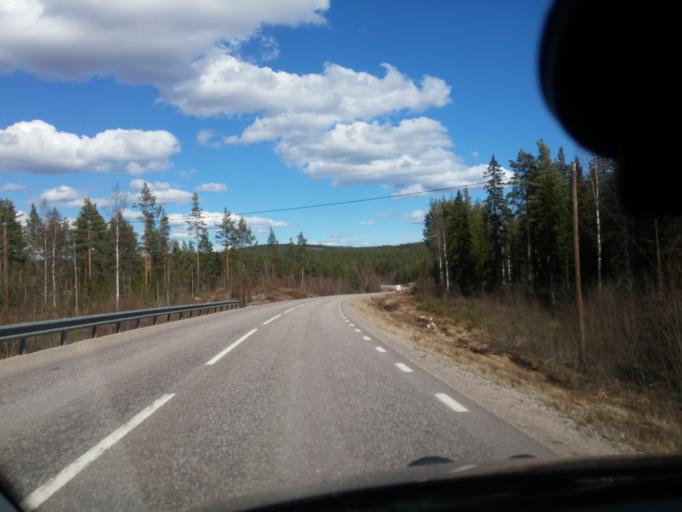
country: SE
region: Gaevleborg
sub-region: Ovanakers Kommun
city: Edsbyn
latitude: 61.2470
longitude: 15.8866
